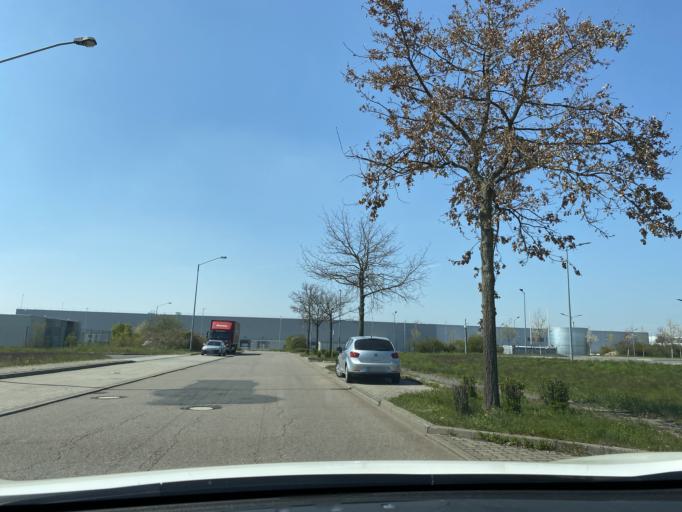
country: DE
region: Saxony
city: Zwochau
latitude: 51.3981
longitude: 12.2935
